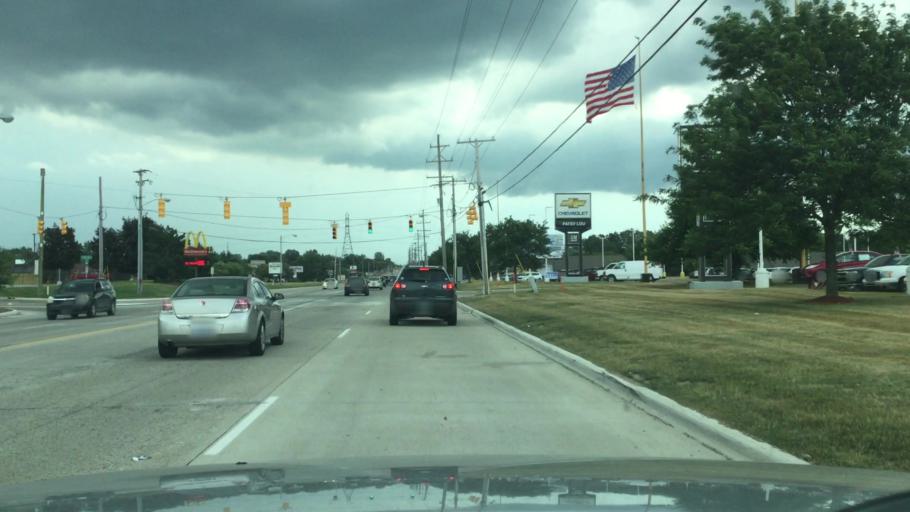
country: US
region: Michigan
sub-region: Genesee County
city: Swartz Creek
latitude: 42.9991
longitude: -83.7727
